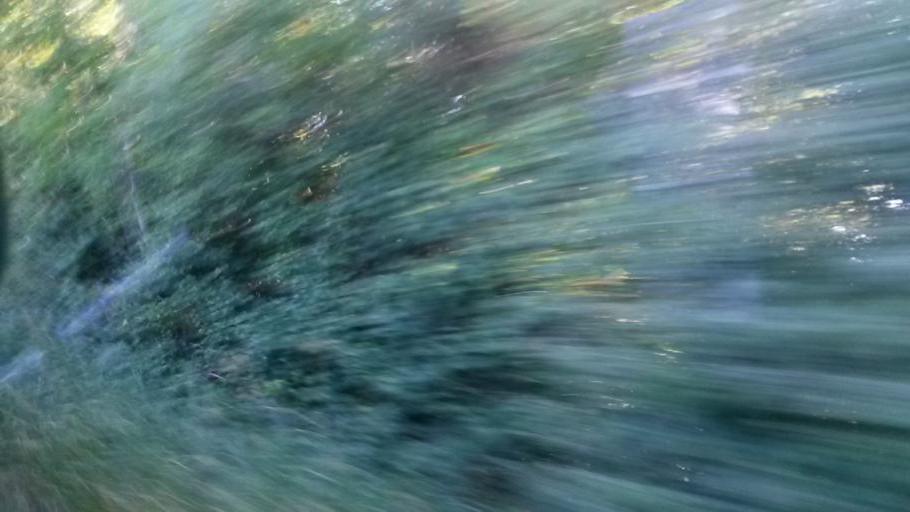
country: IE
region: Leinster
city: Ballymun
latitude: 53.4524
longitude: -6.2944
